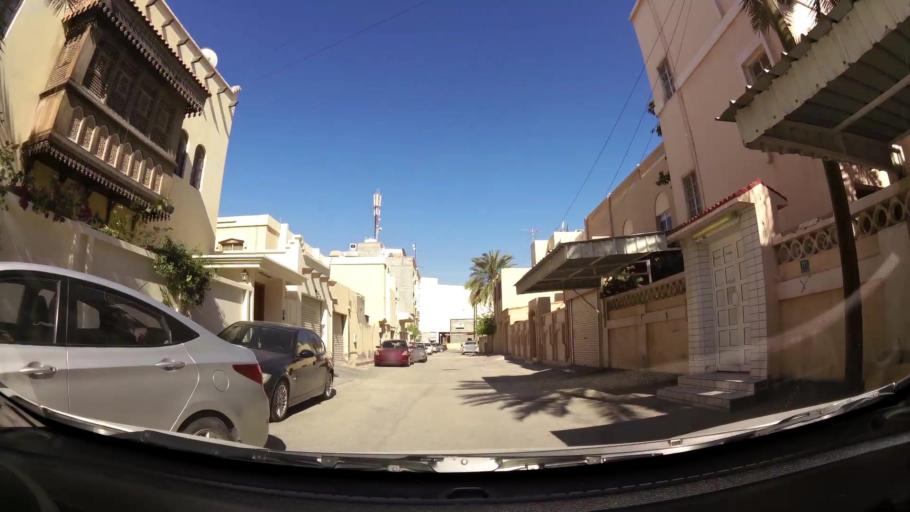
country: BH
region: Muharraq
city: Al Muharraq
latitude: 26.2629
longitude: 50.6173
